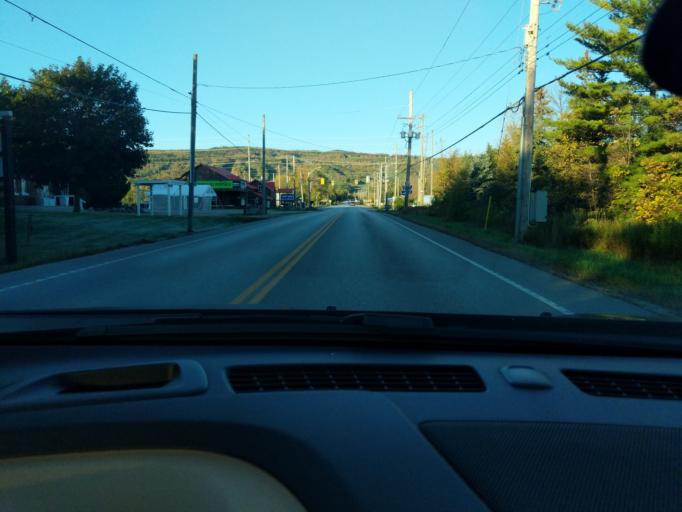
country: CA
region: Ontario
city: Collingwood
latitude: 44.4983
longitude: -80.2839
